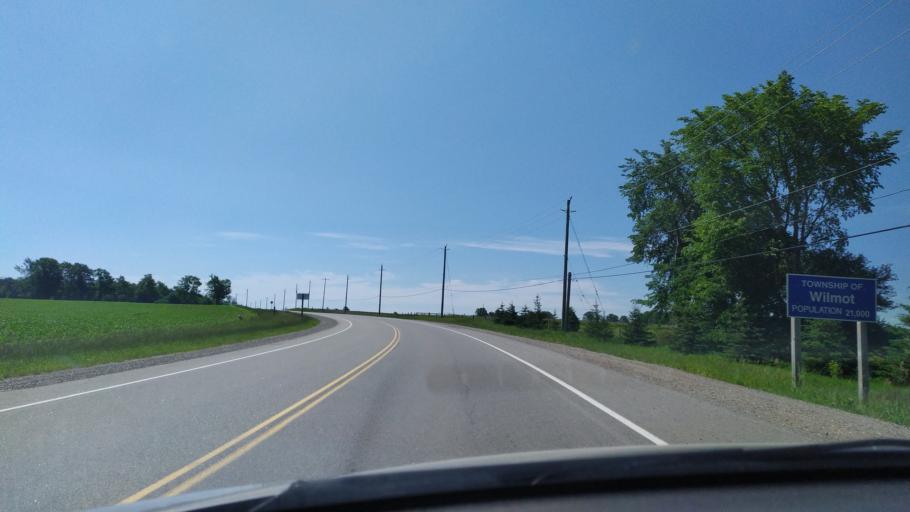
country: CA
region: Ontario
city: Stratford
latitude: 43.4635
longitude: -80.7660
